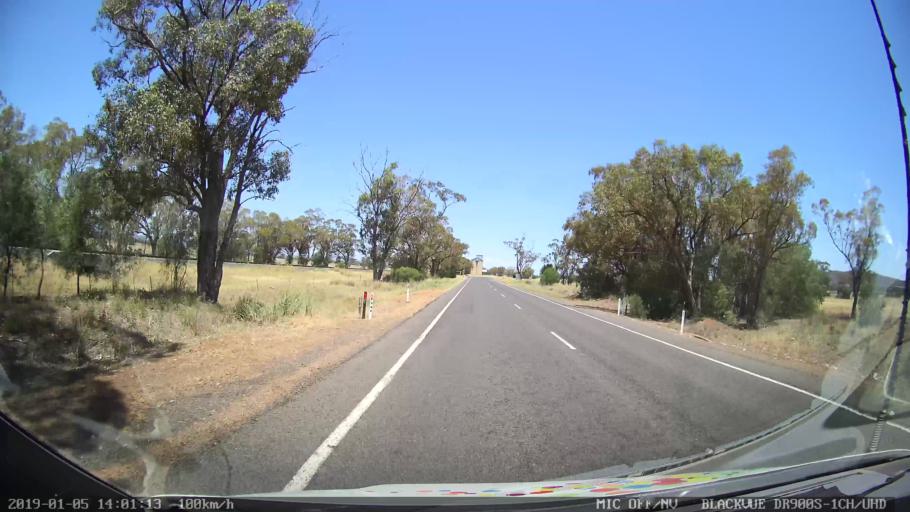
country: AU
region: New South Wales
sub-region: Gunnedah
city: Gunnedah
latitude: -31.1675
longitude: 150.3224
